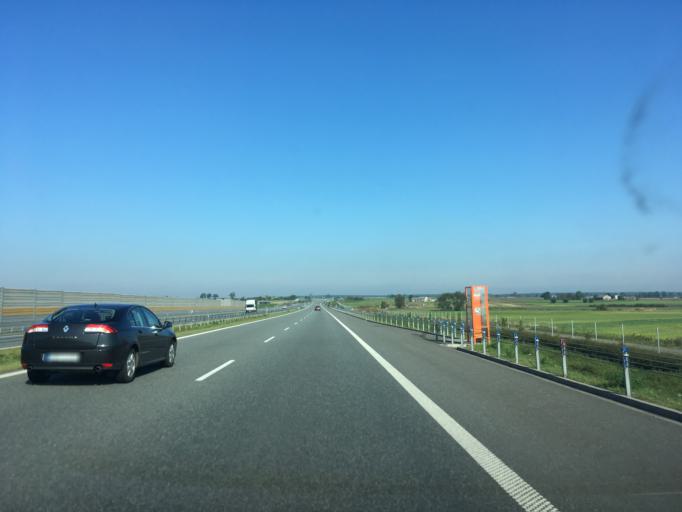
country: PL
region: Kujawsko-Pomorskie
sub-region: Powiat torunski
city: Lubicz Dolny
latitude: 53.1117
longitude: 18.7457
